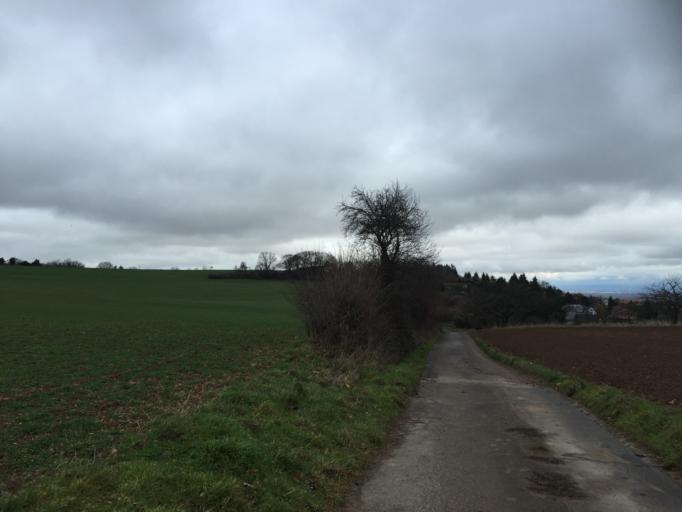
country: DE
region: Rheinland-Pfalz
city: Neuleiningen
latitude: 49.5271
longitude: 8.1273
